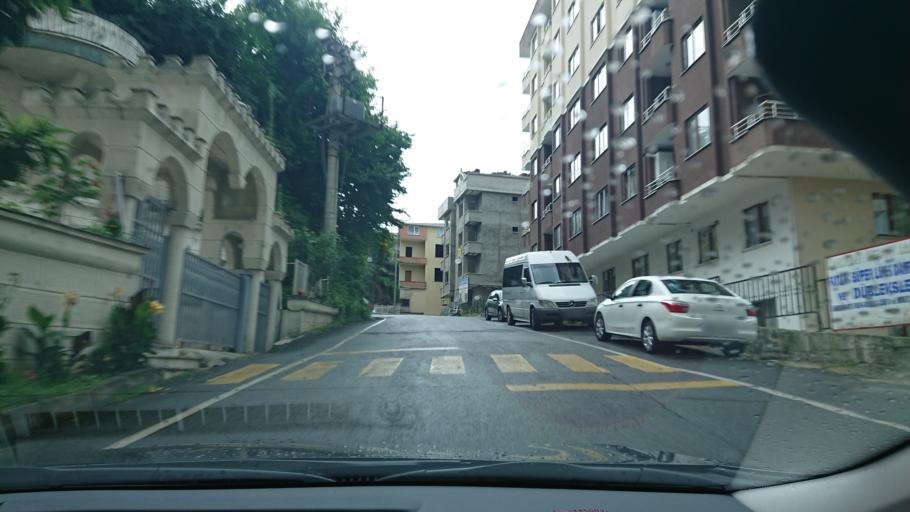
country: TR
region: Rize
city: Rize
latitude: 41.0263
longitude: 40.5113
